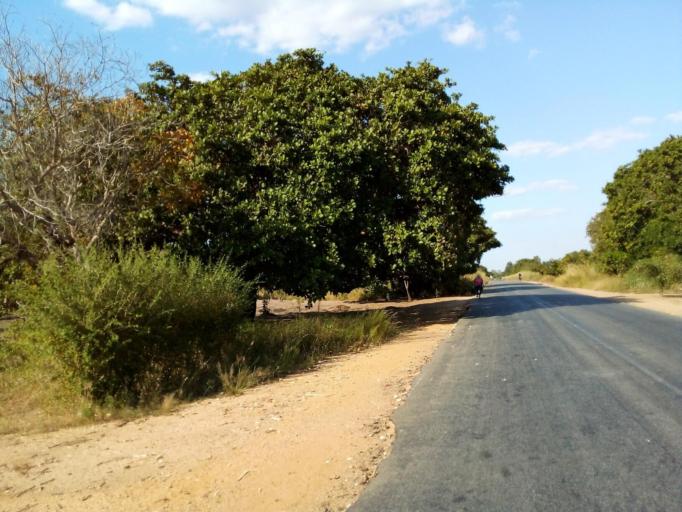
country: MZ
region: Zambezia
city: Quelimane
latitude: -17.5751
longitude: 36.6247
